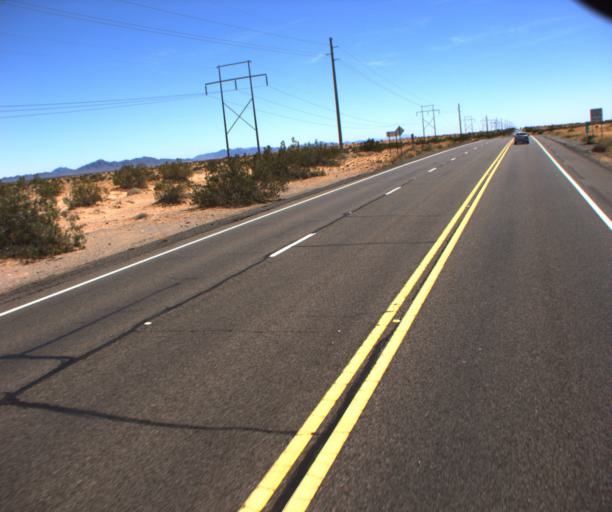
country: US
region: Arizona
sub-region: La Paz County
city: Parker
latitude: 33.9572
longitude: -114.2169
